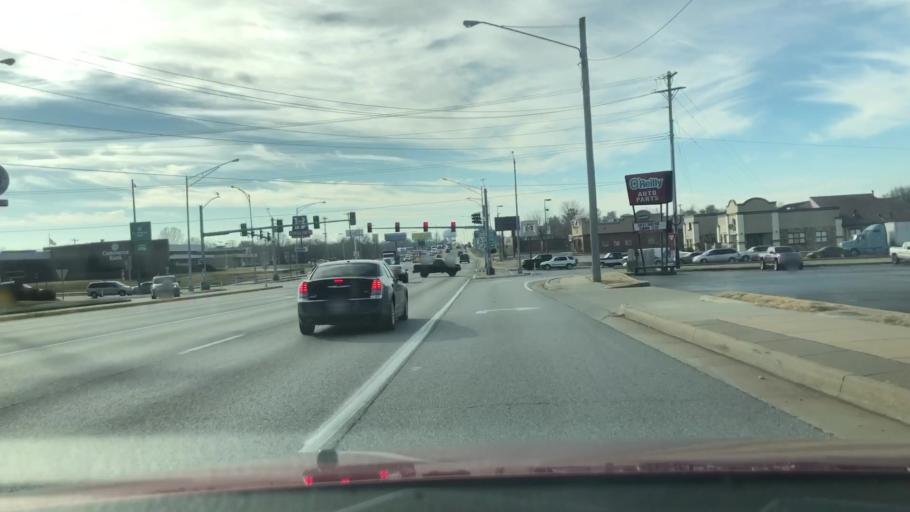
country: US
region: Missouri
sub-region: Greene County
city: Springfield
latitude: 37.2155
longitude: -93.2619
